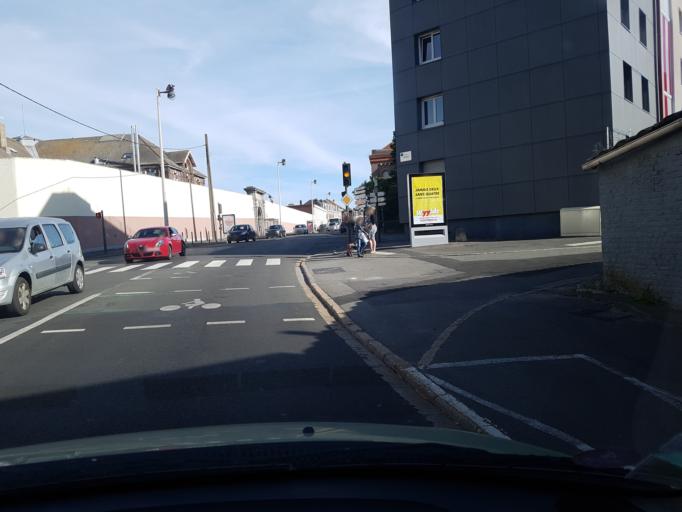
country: FR
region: Nord-Pas-de-Calais
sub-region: Departement du Pas-de-Calais
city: Bethune
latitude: 50.5370
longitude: 2.6360
